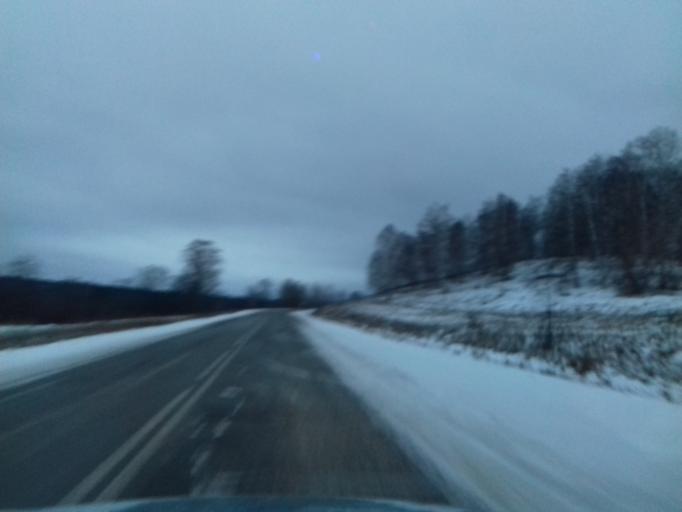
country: RU
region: Bashkortostan
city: Lomovka
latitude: 53.8661
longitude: 58.0686
